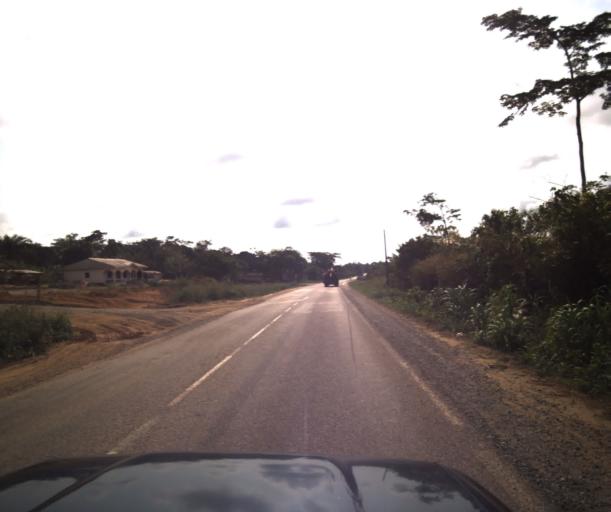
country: CM
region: Littoral
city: Edea
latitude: 3.9502
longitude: 10.0304
